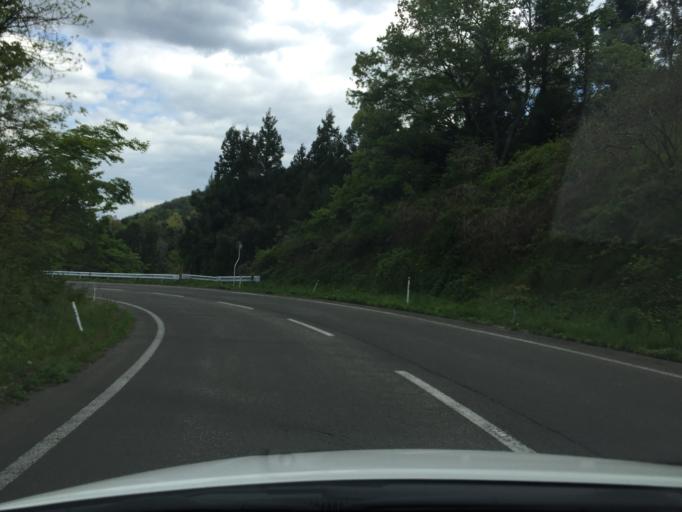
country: JP
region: Fukushima
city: Fukushima-shi
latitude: 37.7167
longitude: 140.5528
